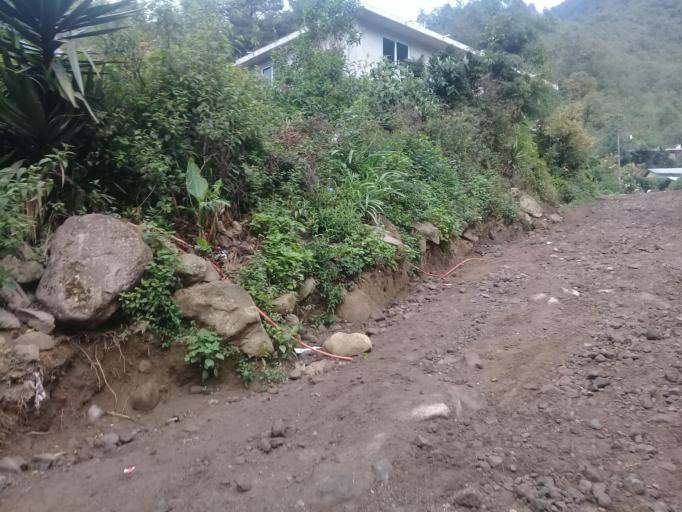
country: MX
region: Veracruz
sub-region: Mariano Escobedo
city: San Isidro el Berro
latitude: 18.9585
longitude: -97.1964
